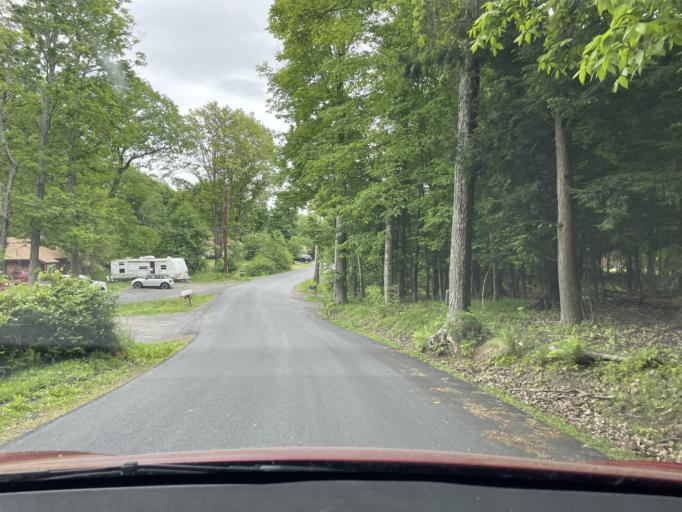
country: US
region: New York
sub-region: Ulster County
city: Woodstock
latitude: 42.0245
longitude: -74.1087
